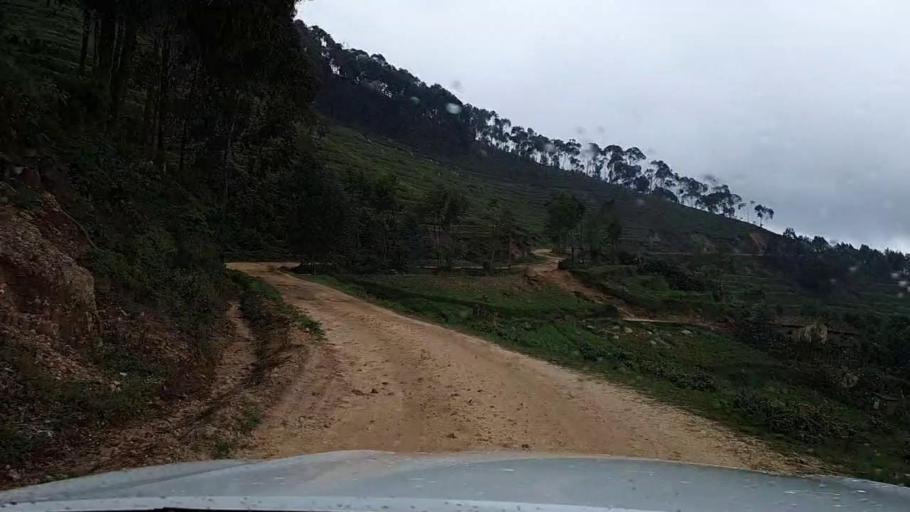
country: RW
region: Western Province
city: Kibuye
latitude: -2.2922
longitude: 29.3816
